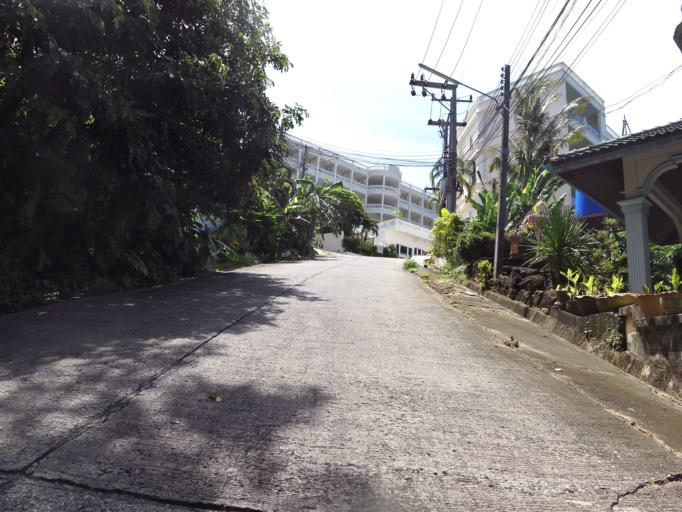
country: TH
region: Phuket
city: Ban Karon
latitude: 7.8474
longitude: 98.3007
